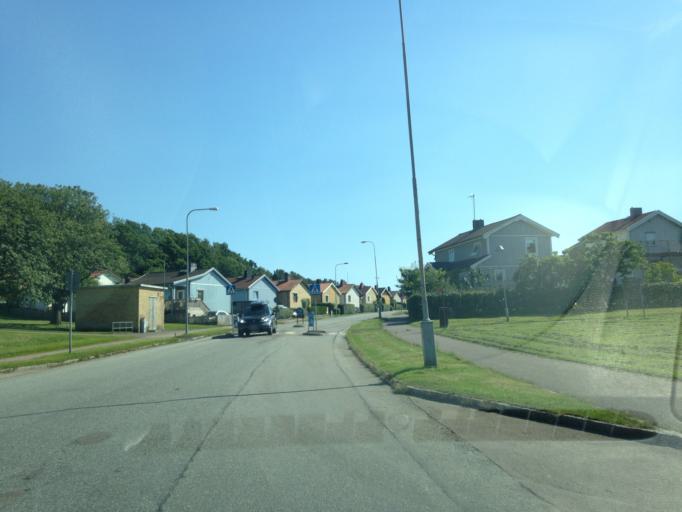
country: SE
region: Vaestra Goetaland
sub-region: Goteborg
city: Majorna
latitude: 57.7287
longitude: 11.9182
